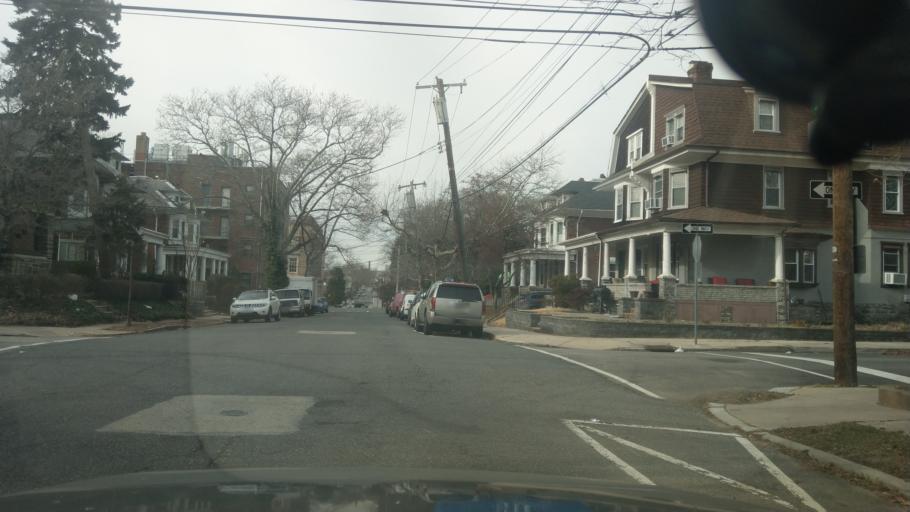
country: US
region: Pennsylvania
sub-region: Montgomery County
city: Wyncote
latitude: 40.0519
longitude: -75.1405
